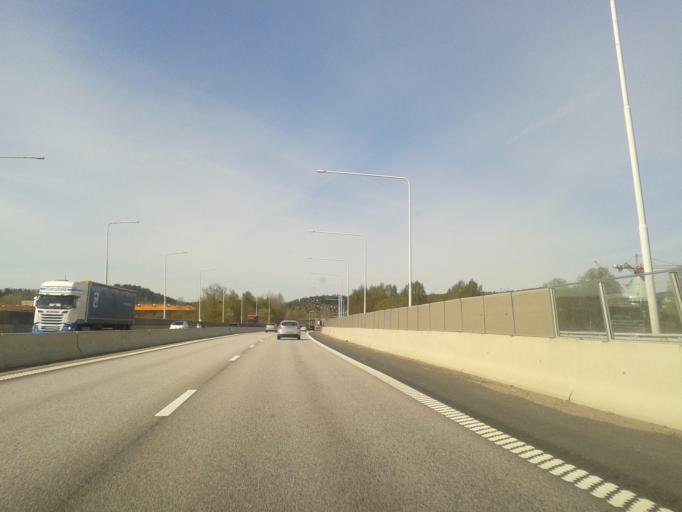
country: SE
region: Vaestra Goetaland
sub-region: Kungalvs Kommun
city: Kungalv
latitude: 57.8669
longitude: 11.9709
